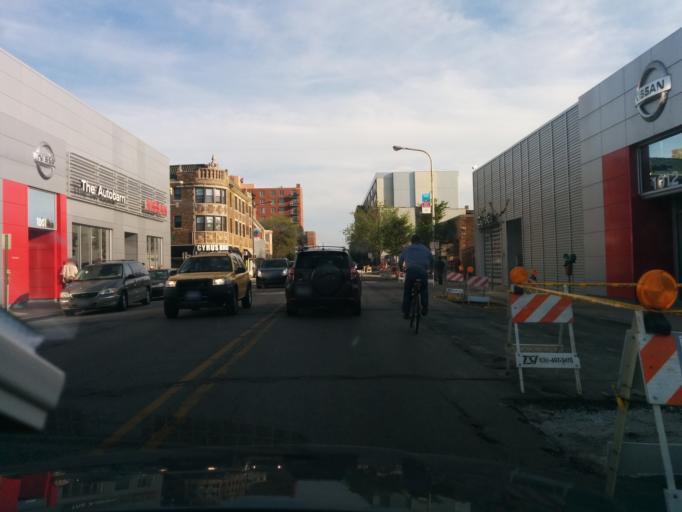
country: US
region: Illinois
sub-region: Cook County
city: Evanston
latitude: 42.0362
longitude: -87.6798
